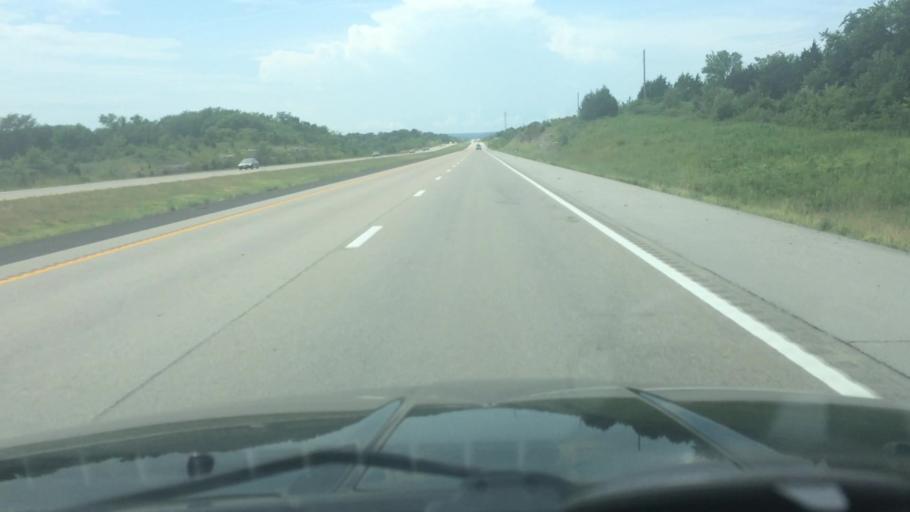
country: US
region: Missouri
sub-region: Polk County
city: Humansville
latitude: 37.7682
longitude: -93.5630
